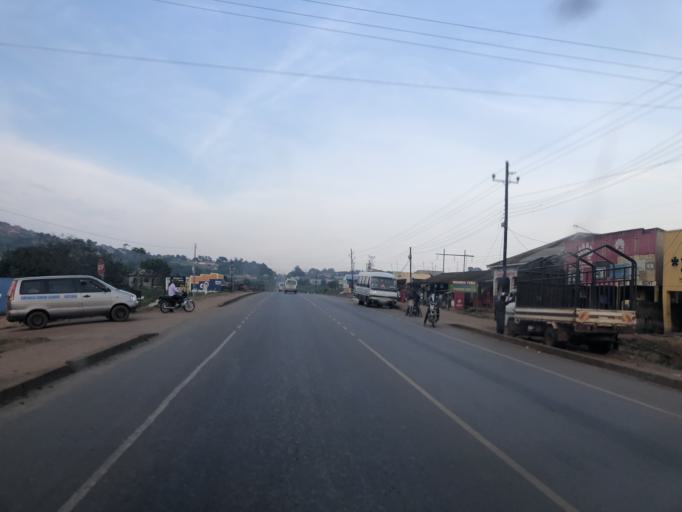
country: UG
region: Central Region
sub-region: Mpigi District
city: Mpigi
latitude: 0.2427
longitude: 32.3654
